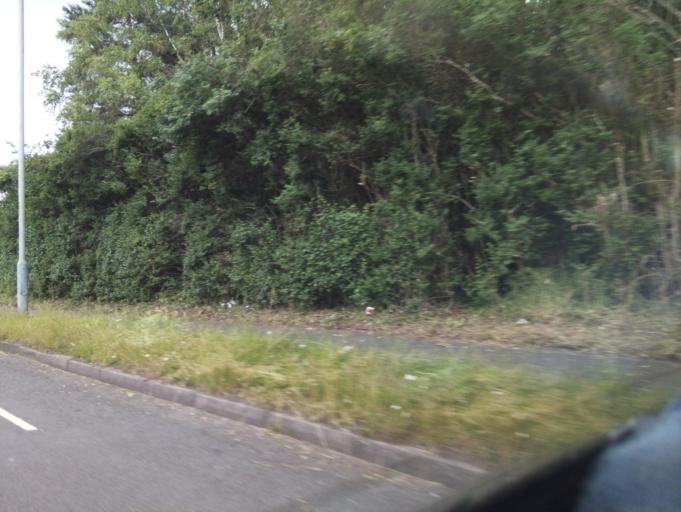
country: GB
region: England
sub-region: Worcestershire
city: Kidderminster
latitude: 52.3760
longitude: -2.2405
